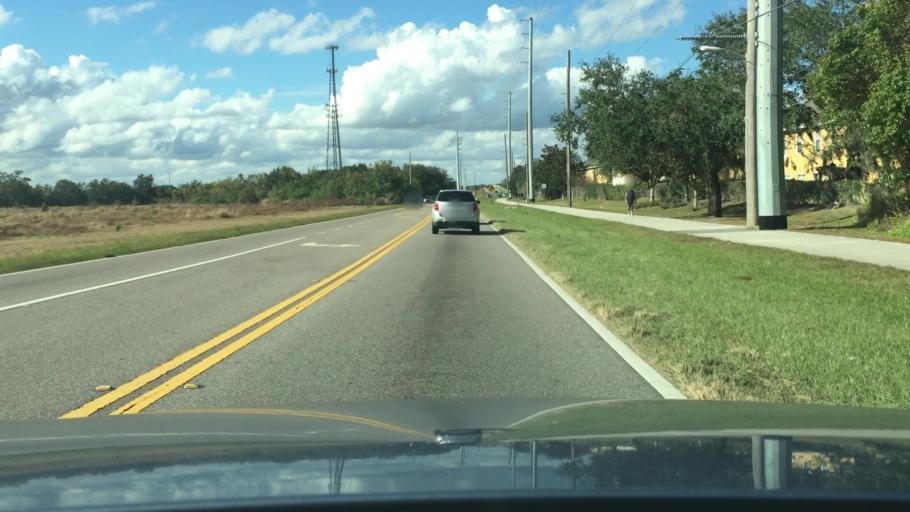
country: US
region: Florida
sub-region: Osceola County
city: Saint Cloud
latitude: 28.2514
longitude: -81.3223
